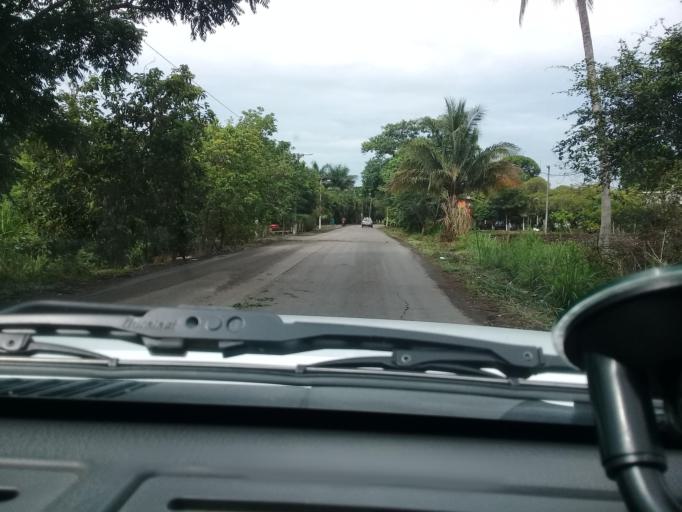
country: MX
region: Veracruz
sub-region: Paso de Ovejas
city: El Hatito
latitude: 19.3207
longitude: -96.3749
